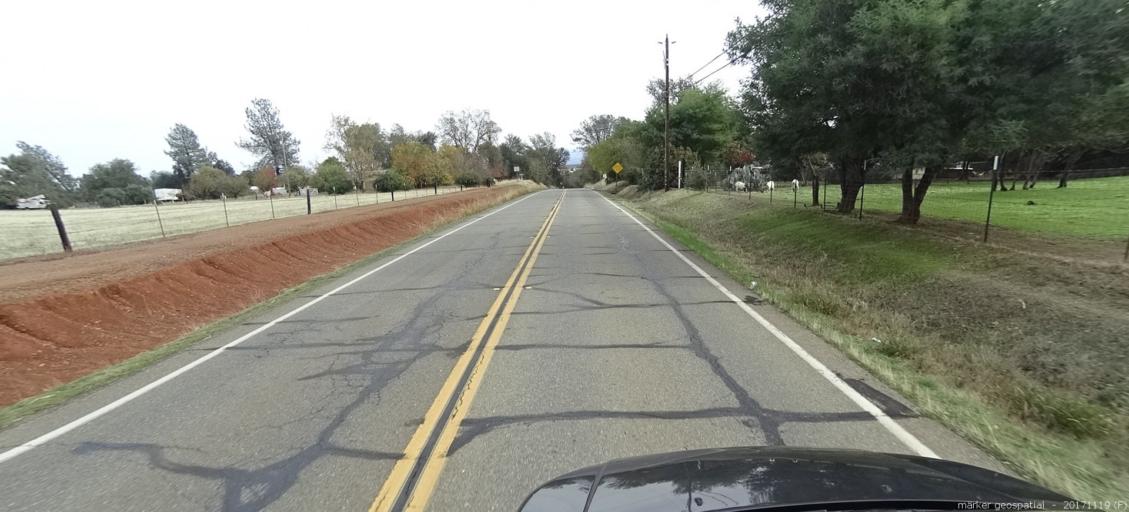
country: US
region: California
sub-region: Shasta County
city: Anderson
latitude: 40.4804
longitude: -122.2659
